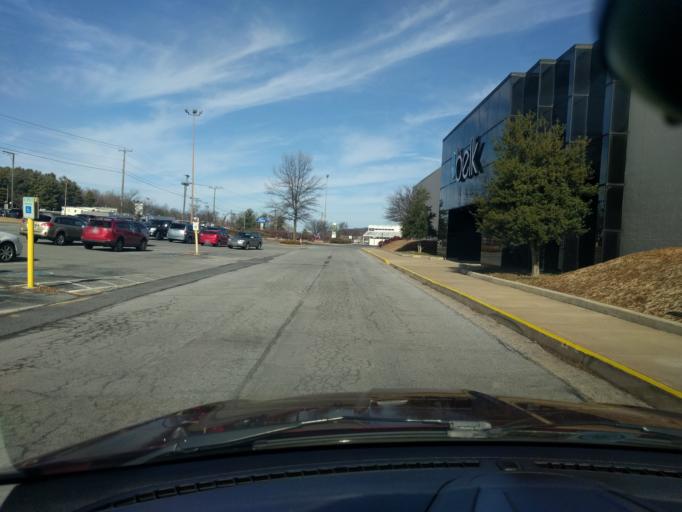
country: US
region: Virginia
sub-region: Augusta County
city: Jolivue
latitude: 38.1258
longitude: -79.0638
